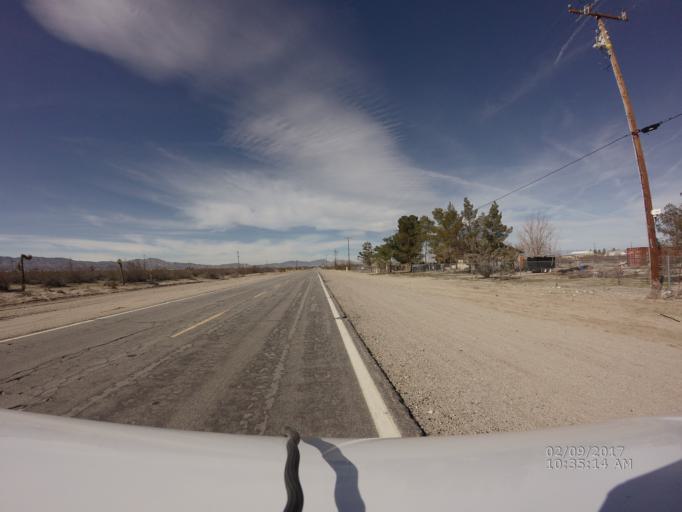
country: US
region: California
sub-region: Los Angeles County
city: Littlerock
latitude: 34.5428
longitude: -117.9207
